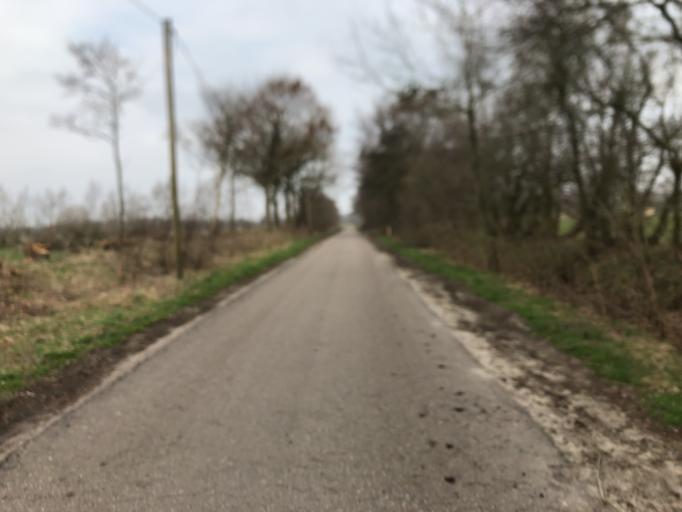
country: DE
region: Schleswig-Holstein
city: Wanderup
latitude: 54.6793
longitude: 9.3367
